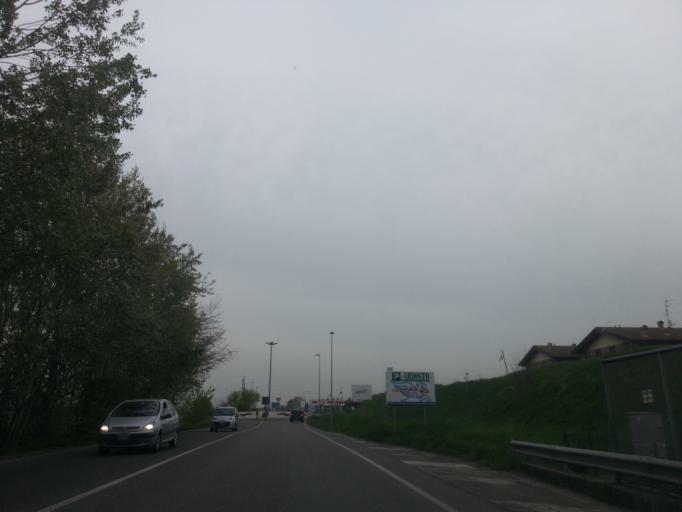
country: IT
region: Emilia-Romagna
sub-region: Provincia di Reggio Emilia
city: Reggio nell'Emilia
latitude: 44.6736
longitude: 10.6016
